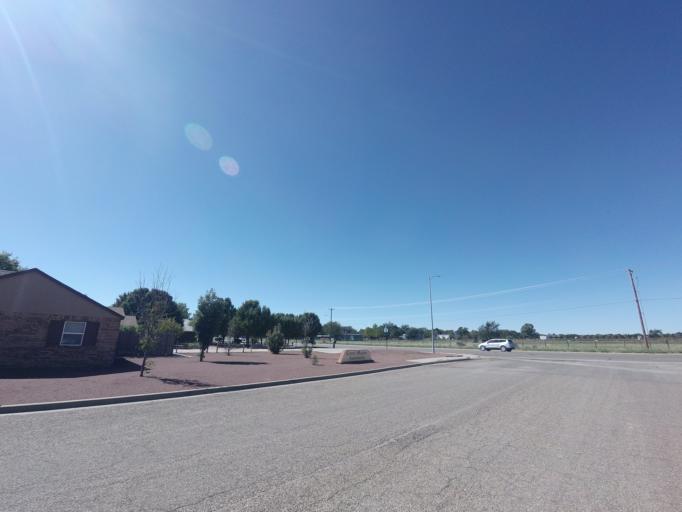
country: US
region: New Mexico
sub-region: Curry County
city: Clovis
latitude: 34.4216
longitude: -103.1782
